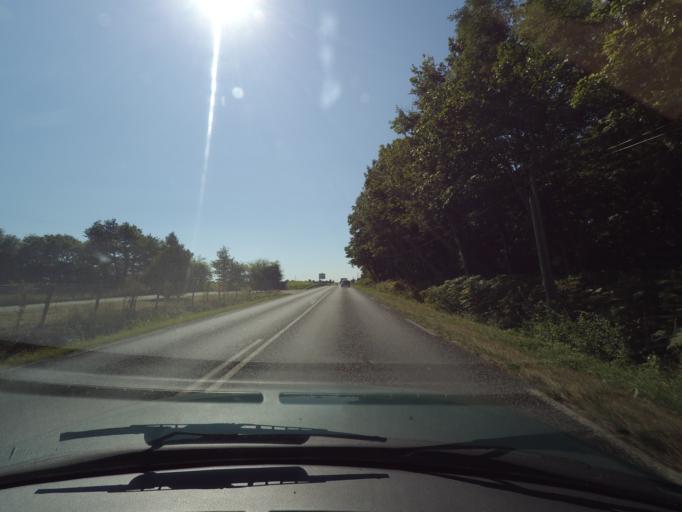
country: FR
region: Limousin
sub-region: Departement de la Haute-Vienne
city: Bellac
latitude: 46.0838
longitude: 1.0874
